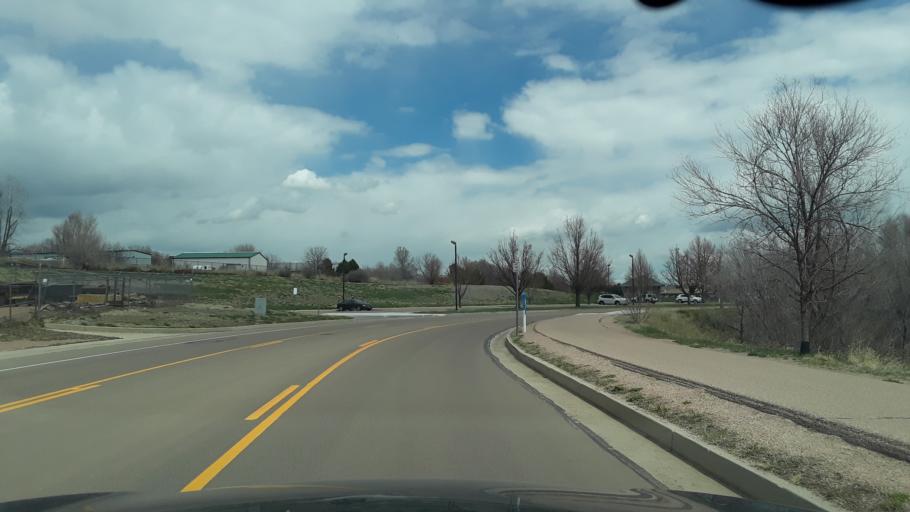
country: US
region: Colorado
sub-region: El Paso County
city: Colorado Springs
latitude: 38.8846
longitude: -104.8295
